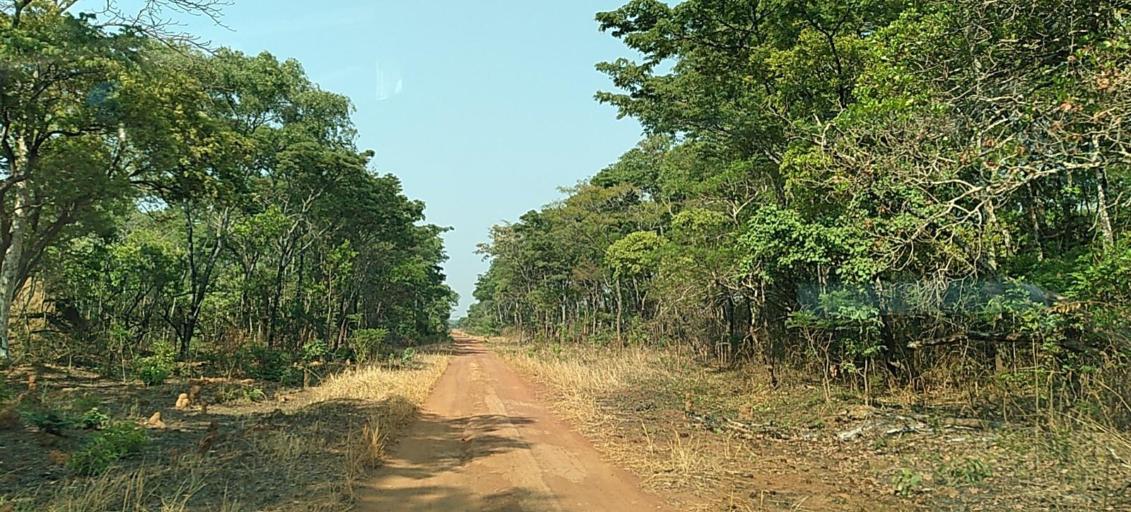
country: ZM
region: Copperbelt
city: Chingola
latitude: -12.8824
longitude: 27.4278
